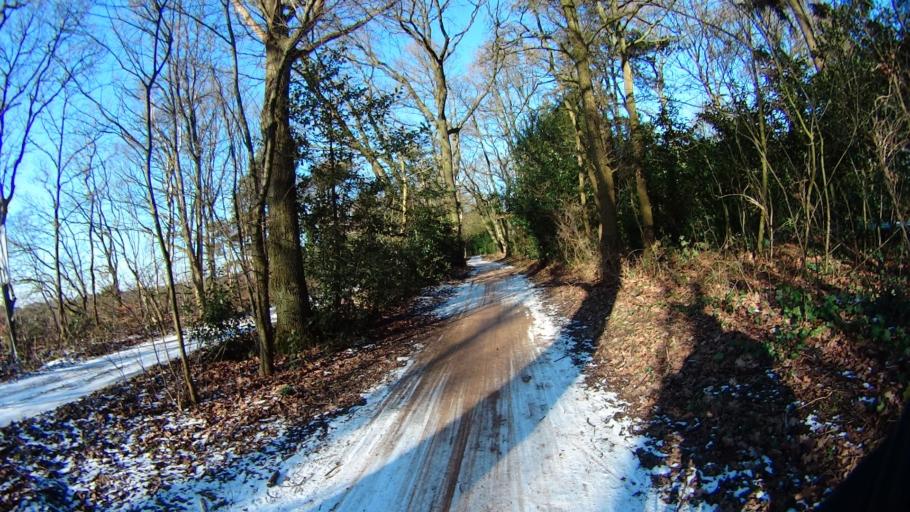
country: NL
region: North Holland
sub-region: Gemeente Laren
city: Laren
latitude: 52.2489
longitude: 5.2052
